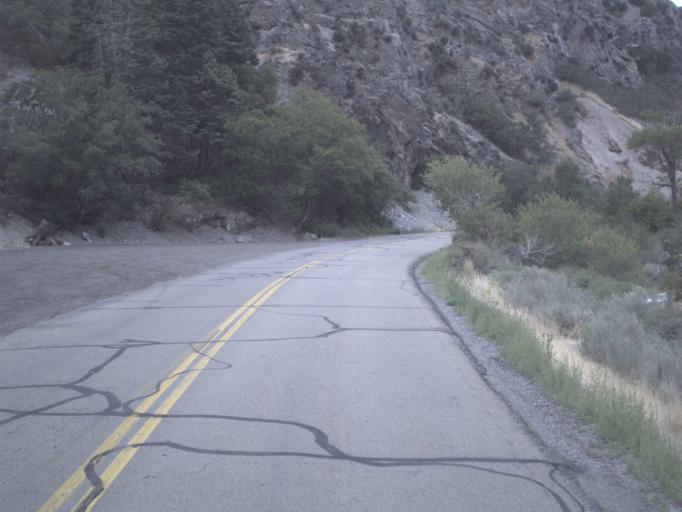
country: US
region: Utah
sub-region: Utah County
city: Cedar Hills
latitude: 40.4328
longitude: -111.7480
